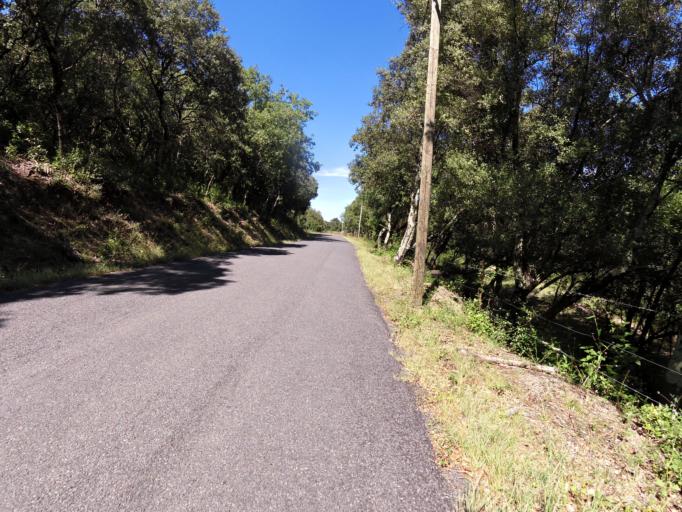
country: FR
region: Languedoc-Roussillon
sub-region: Departement du Gard
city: Quissac
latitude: 43.9315
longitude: 4.0477
